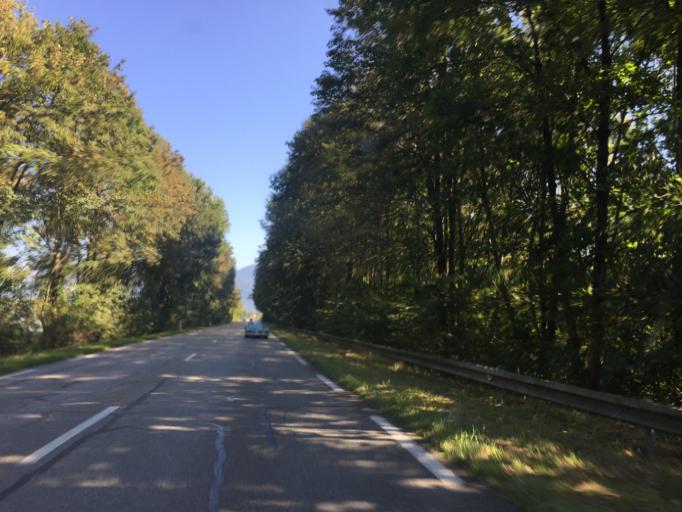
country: FR
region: Rhone-Alpes
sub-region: Departement de la Savoie
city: Frontenex
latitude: 45.6217
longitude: 6.3110
